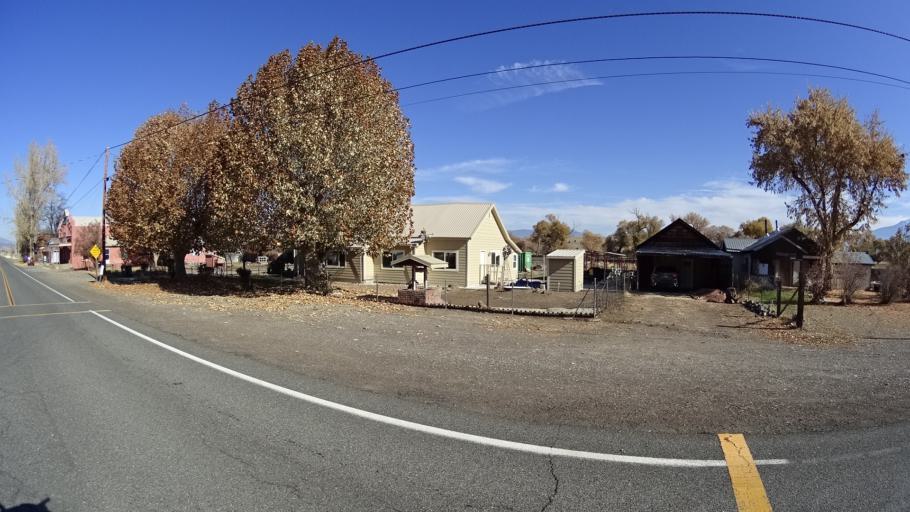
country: US
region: California
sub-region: Siskiyou County
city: Weed
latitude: 41.5210
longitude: -122.5200
